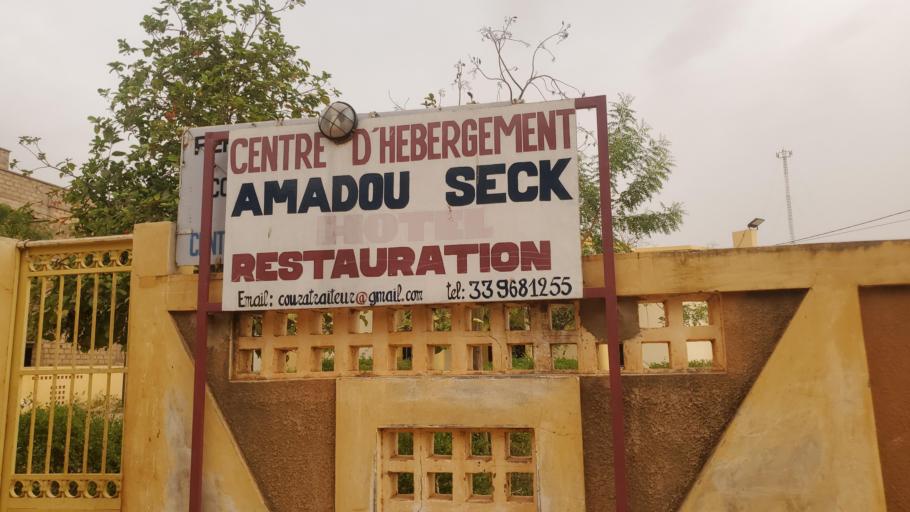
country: SN
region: Louga
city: Ndibene Dahra
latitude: 15.3970
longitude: -15.1156
